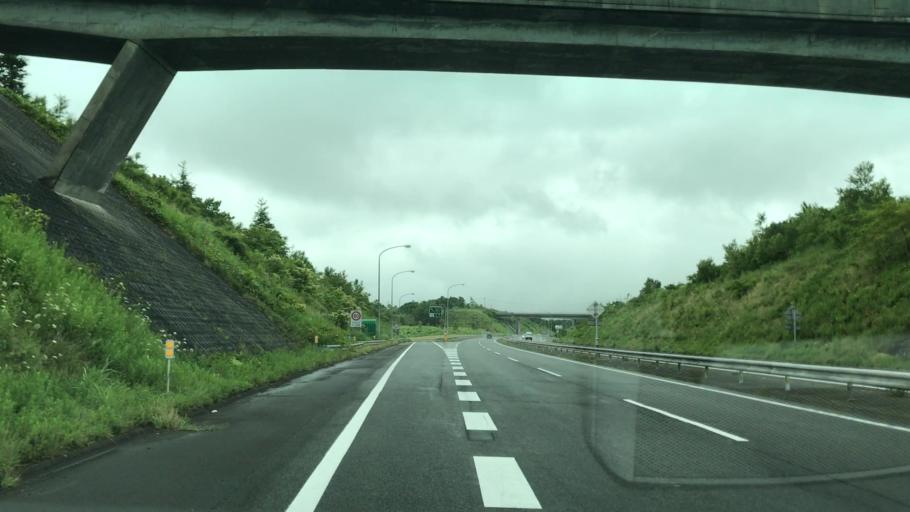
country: JP
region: Hokkaido
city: Muroran
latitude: 42.3863
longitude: 140.9751
